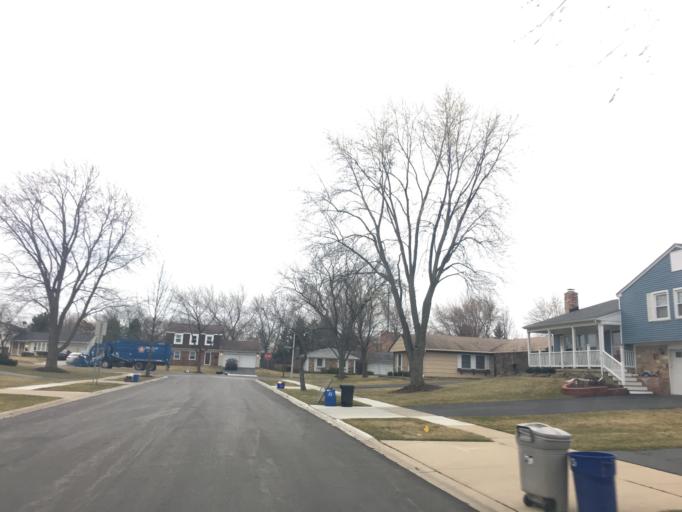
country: US
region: Illinois
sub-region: Cook County
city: Schaumburg
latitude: 42.0280
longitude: -88.1199
